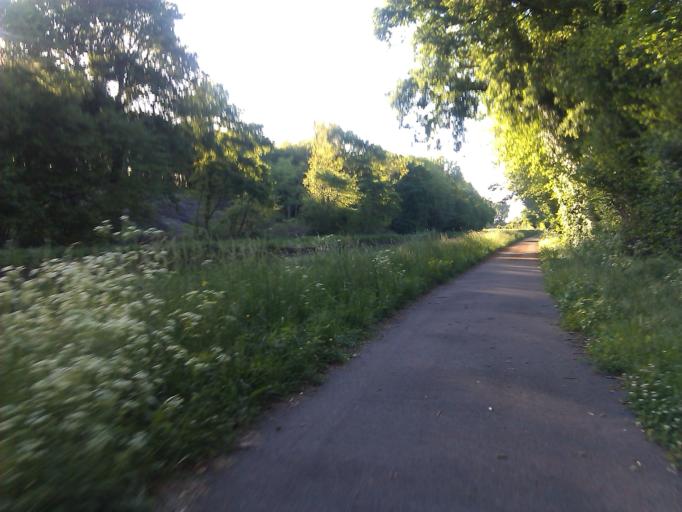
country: FR
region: Auvergne
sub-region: Departement de l'Allier
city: Dompierre-sur-Besbre
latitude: 46.5340
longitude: 3.7157
